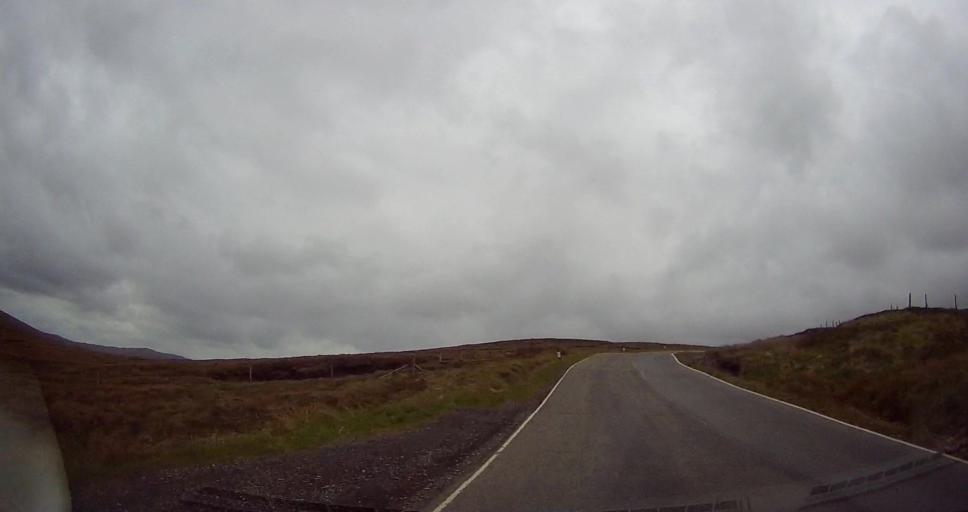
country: GB
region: Scotland
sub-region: Shetland Islands
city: Lerwick
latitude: 60.2776
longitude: -1.2579
